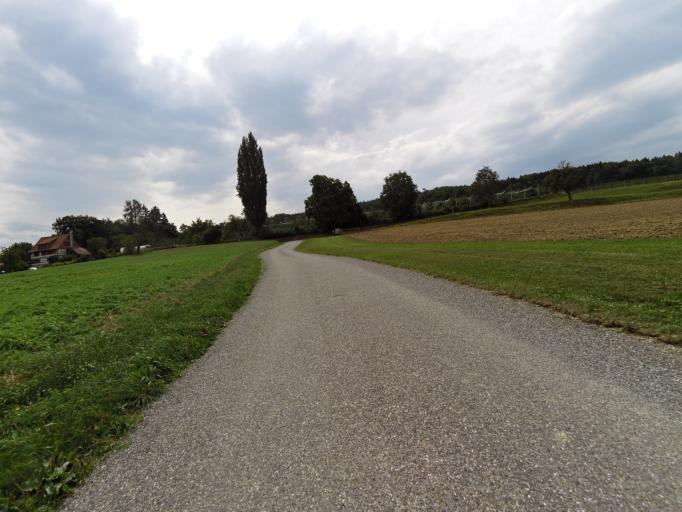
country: CH
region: Thurgau
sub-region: Kreuzlingen District
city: Ermatingen
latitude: 47.6591
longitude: 9.0620
